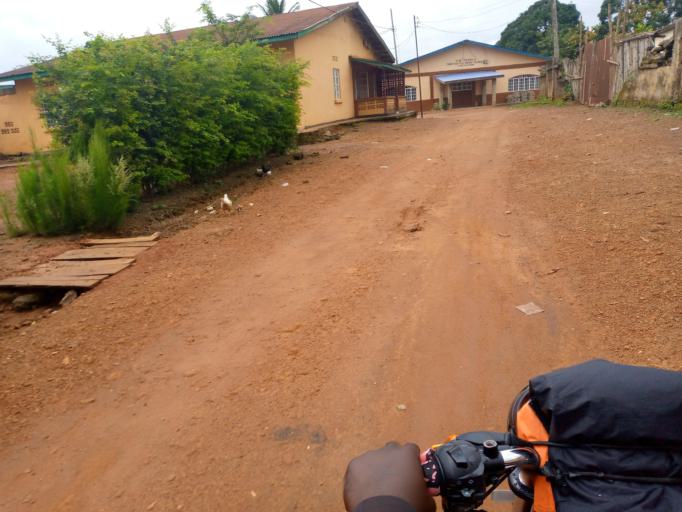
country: SL
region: Eastern Province
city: Kenema
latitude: 7.8702
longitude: -11.1830
